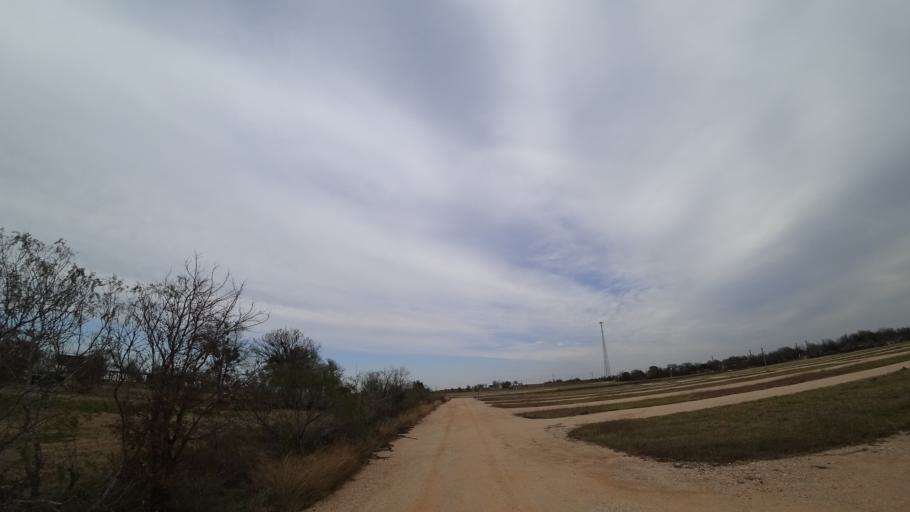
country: US
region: Texas
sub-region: Travis County
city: Garfield
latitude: 30.1364
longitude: -97.6223
